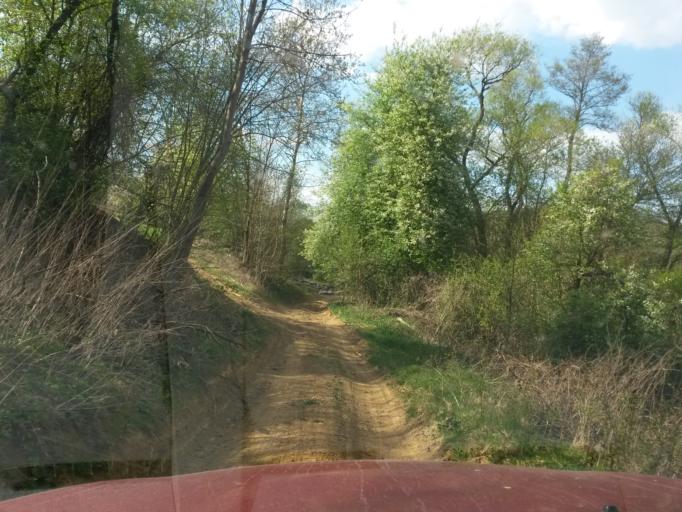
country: SK
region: Presovsky
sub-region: Okres Presov
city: Presov
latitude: 48.9544
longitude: 21.1512
